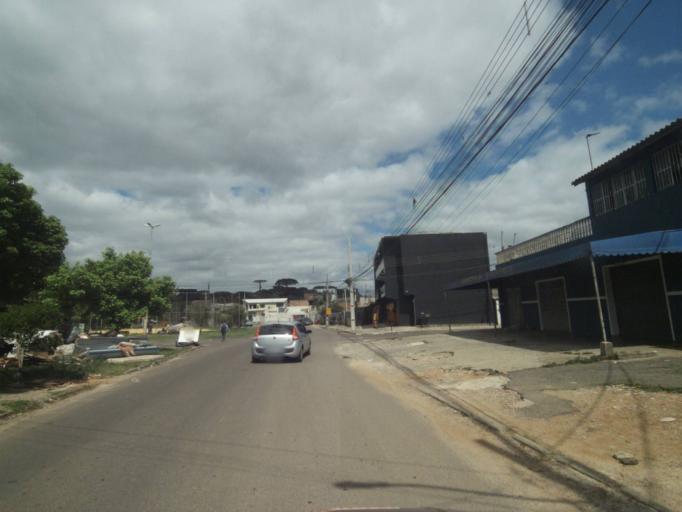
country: BR
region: Parana
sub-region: Sao Jose Dos Pinhais
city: Sao Jose dos Pinhais
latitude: -25.5545
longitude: -49.2644
